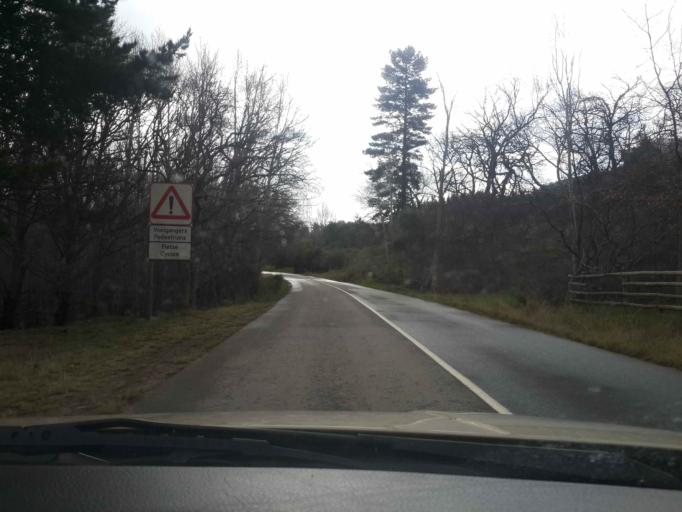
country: ZA
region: Western Cape
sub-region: Cape Winelands District Municipality
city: Stellenbosch
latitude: -33.9667
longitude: 18.9328
